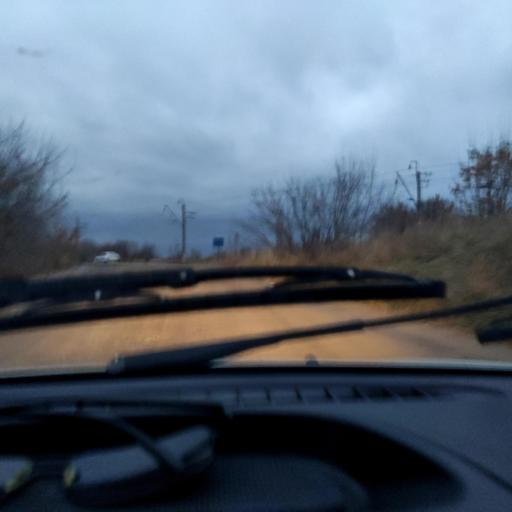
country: RU
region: Samara
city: Tol'yatti
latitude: 53.5676
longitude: 49.4833
